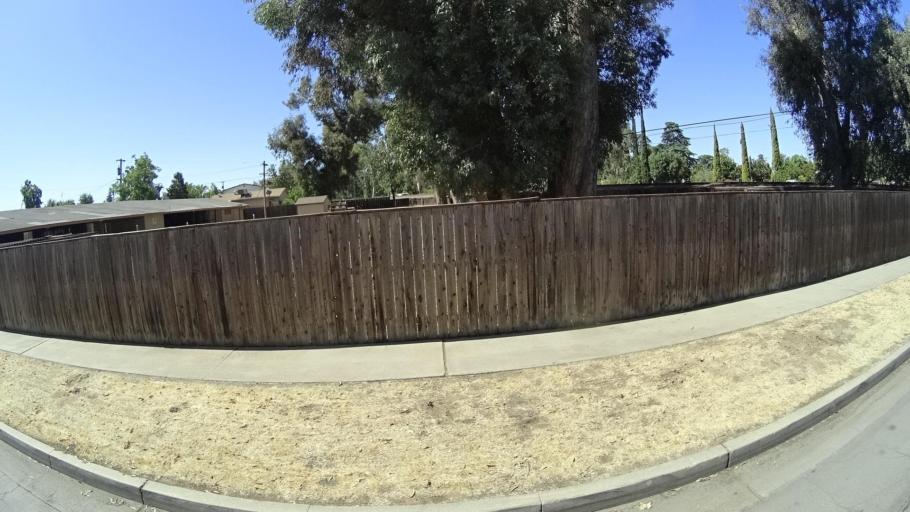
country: US
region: California
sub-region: Fresno County
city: Fresno
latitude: 36.7812
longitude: -119.8032
